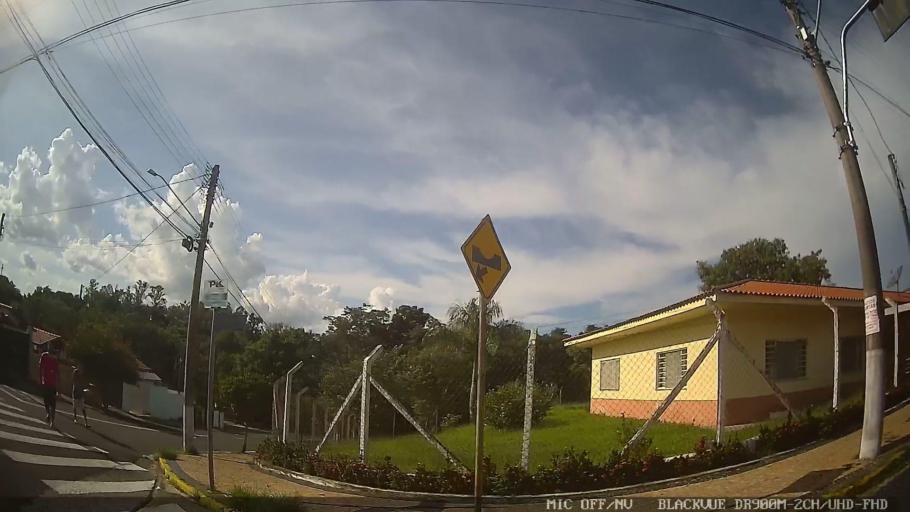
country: BR
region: Sao Paulo
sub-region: Laranjal Paulista
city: Laranjal Paulista
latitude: -23.0838
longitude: -47.7938
